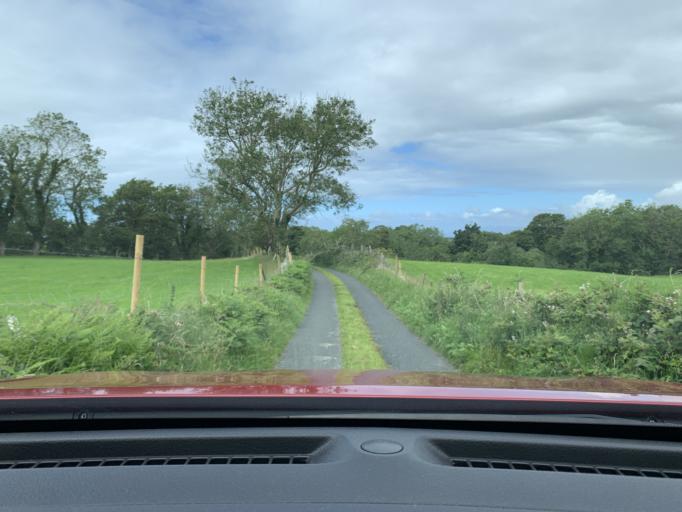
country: IE
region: Connaught
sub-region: Sligo
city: Sligo
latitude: 54.3805
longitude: -8.5061
